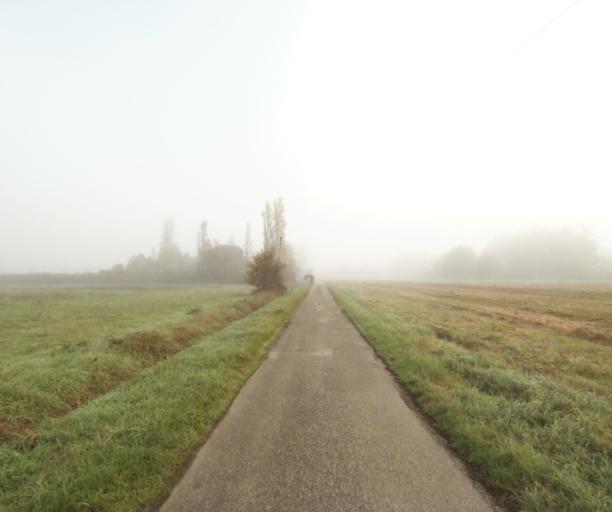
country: FR
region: Midi-Pyrenees
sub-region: Departement du Tarn-et-Garonne
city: Nohic
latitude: 43.8967
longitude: 1.4439
